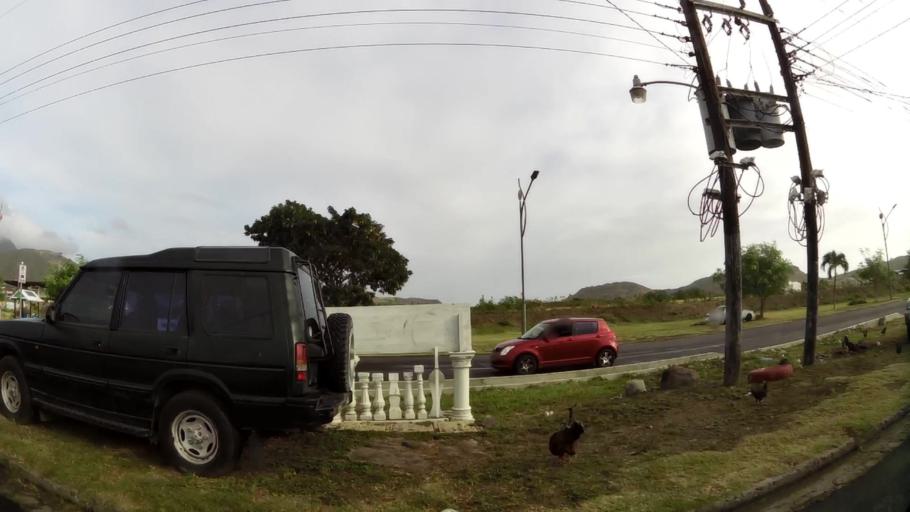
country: KN
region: Saint George Basseterre
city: Basseterre
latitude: 17.2967
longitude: -62.7153
